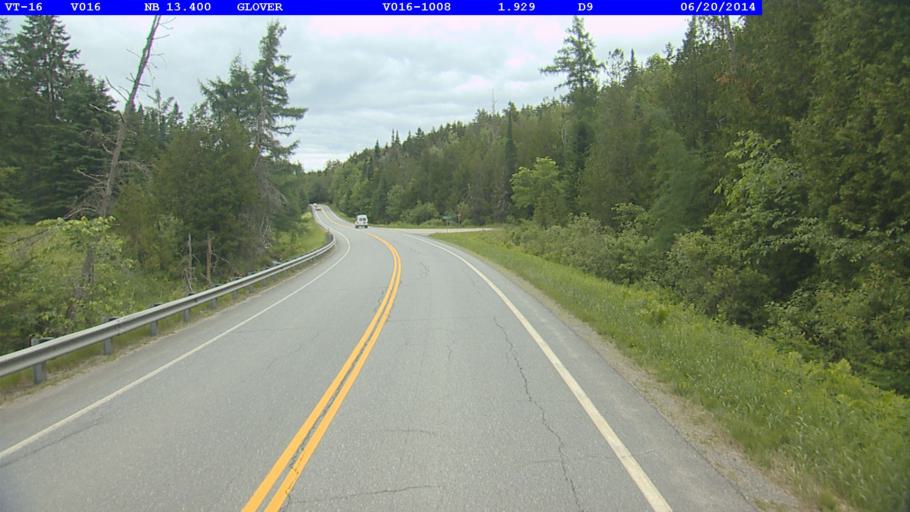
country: US
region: Vermont
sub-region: Caledonia County
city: Hardwick
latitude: 44.6519
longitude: -72.1979
